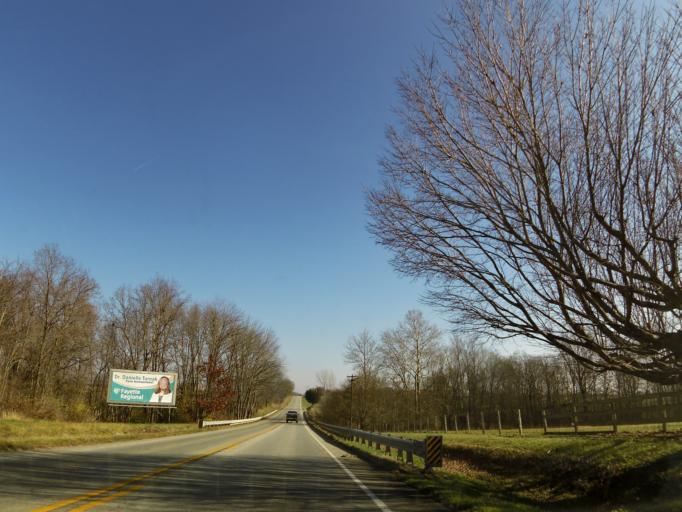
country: US
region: Indiana
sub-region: Fayette County
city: Connersville
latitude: 39.6361
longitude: -85.1897
